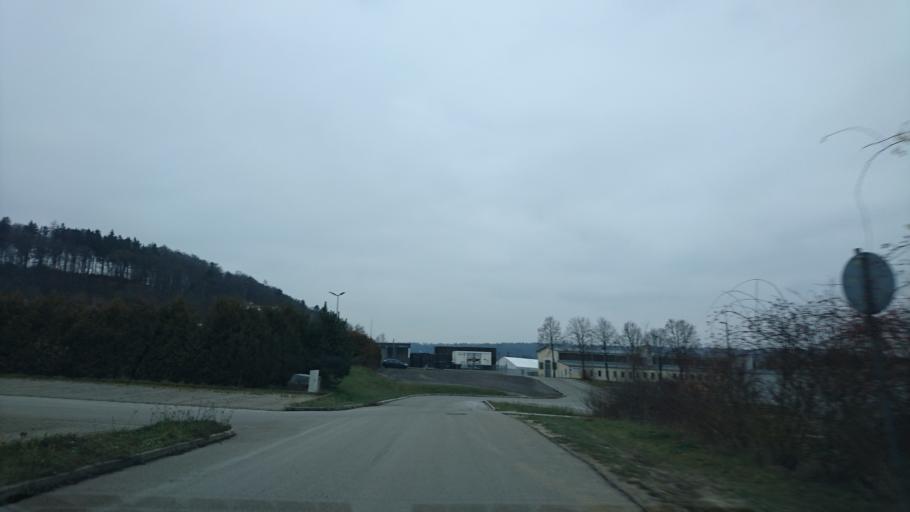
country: DE
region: Bavaria
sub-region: Swabia
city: Zusmarshausen
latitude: 48.4080
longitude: 10.6039
